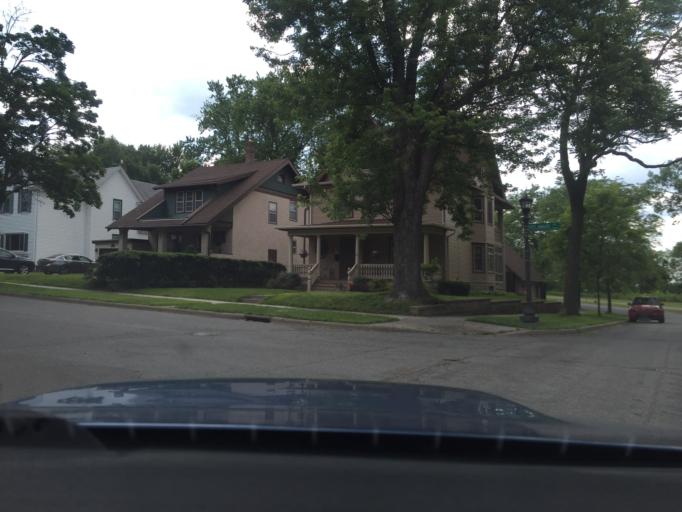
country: US
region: Minnesota
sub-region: Dakota County
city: West Saint Paul
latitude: 44.9266
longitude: -93.1058
